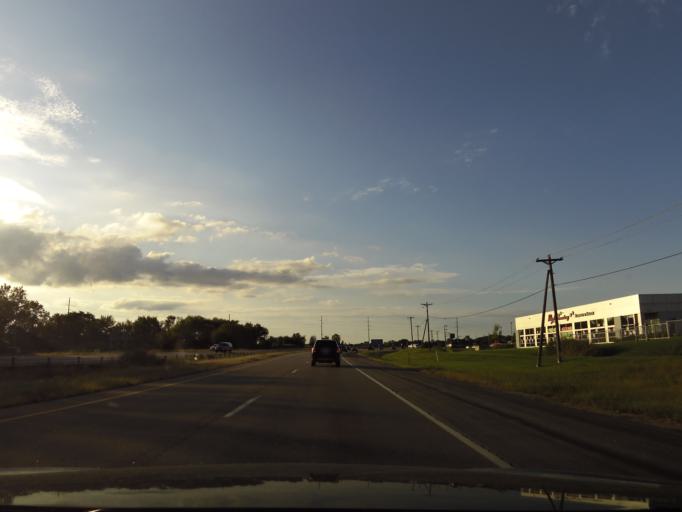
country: US
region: Minnesota
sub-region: Dakota County
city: Hastings
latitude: 44.7682
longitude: -92.8607
